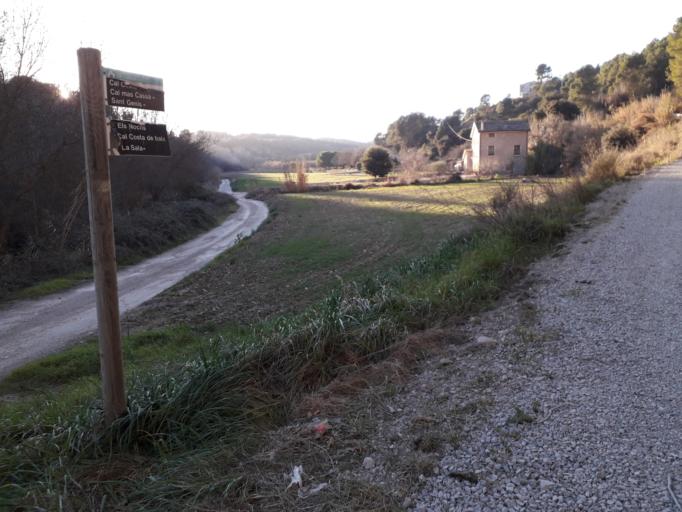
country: ES
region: Catalonia
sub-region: Provincia de Barcelona
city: Jorba
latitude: 41.5874
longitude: 1.5729
